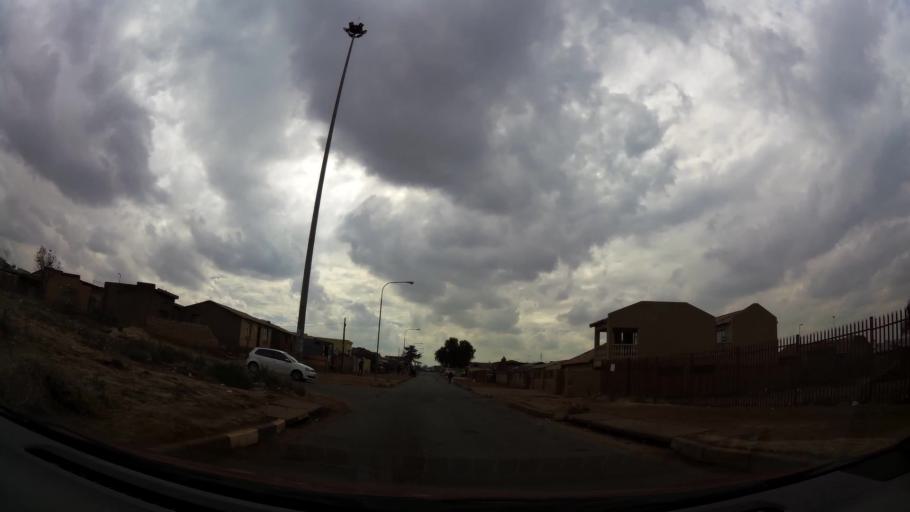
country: ZA
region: Gauteng
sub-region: City of Johannesburg Metropolitan Municipality
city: Soweto
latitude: -26.2615
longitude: 27.8320
